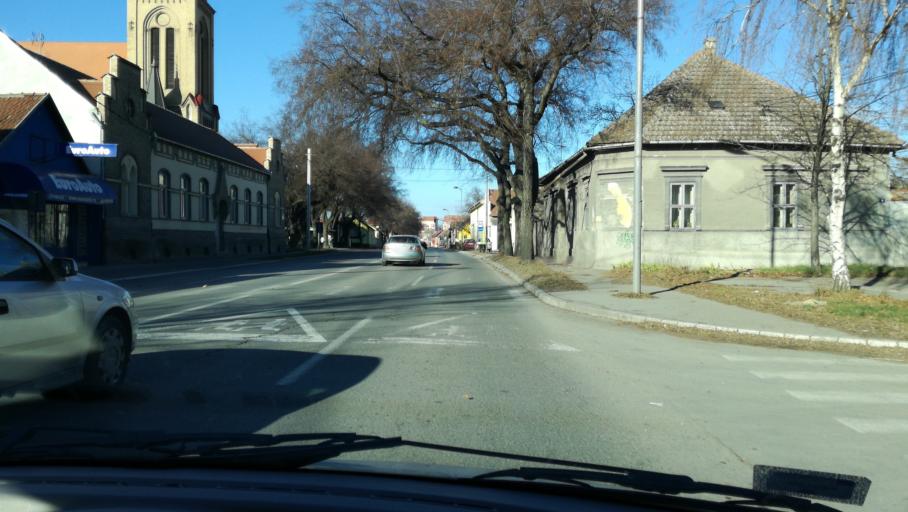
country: RS
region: Autonomna Pokrajina Vojvodina
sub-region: Severnobacki Okrug
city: Subotica
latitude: 46.0889
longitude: 19.6667
